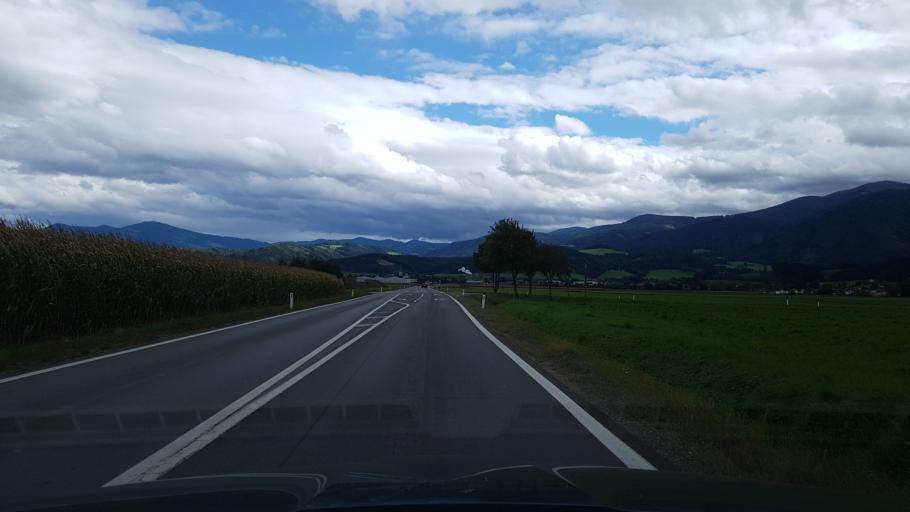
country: AT
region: Styria
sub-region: Politischer Bezirk Murtal
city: Weisskirchen in Steiermark
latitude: 47.1616
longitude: 14.7059
